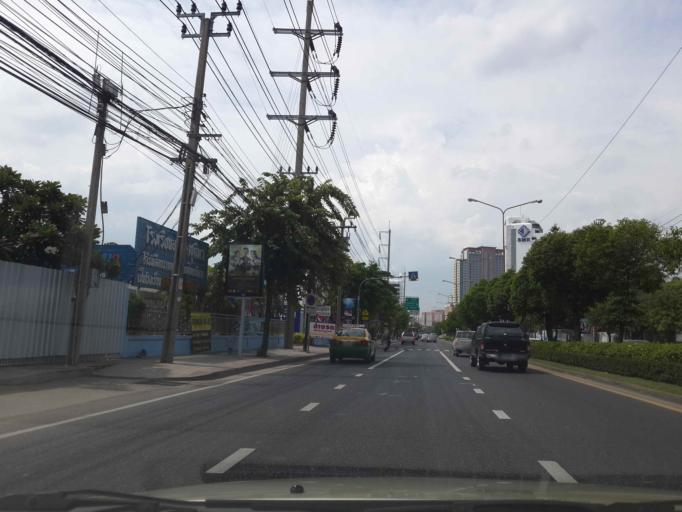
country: TH
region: Bangkok
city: Bang Kapi
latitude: 13.7472
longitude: 100.6437
